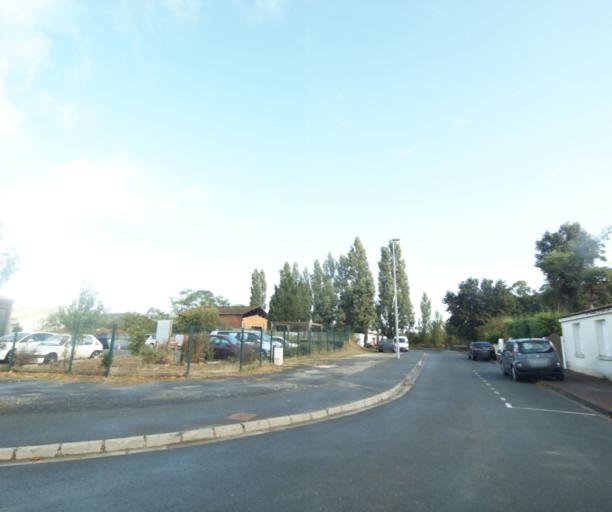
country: FR
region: Poitou-Charentes
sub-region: Departement de la Charente-Maritime
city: Breuil-Magne
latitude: 45.9527
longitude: -0.9418
